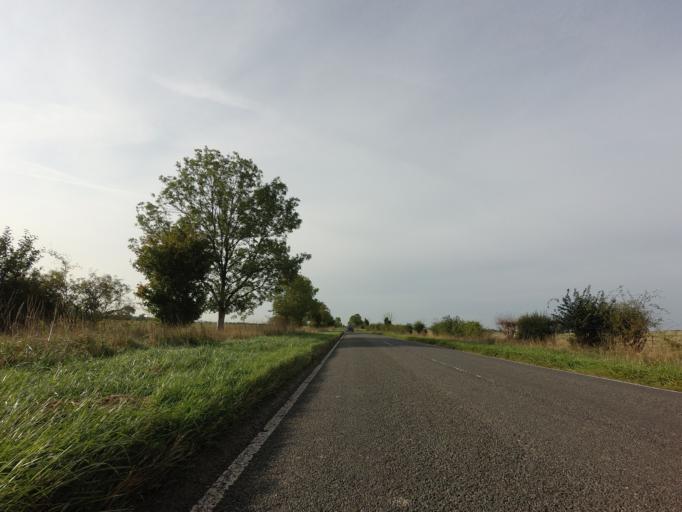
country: GB
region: England
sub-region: Cambridgeshire
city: Harston
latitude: 52.1089
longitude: 0.0890
